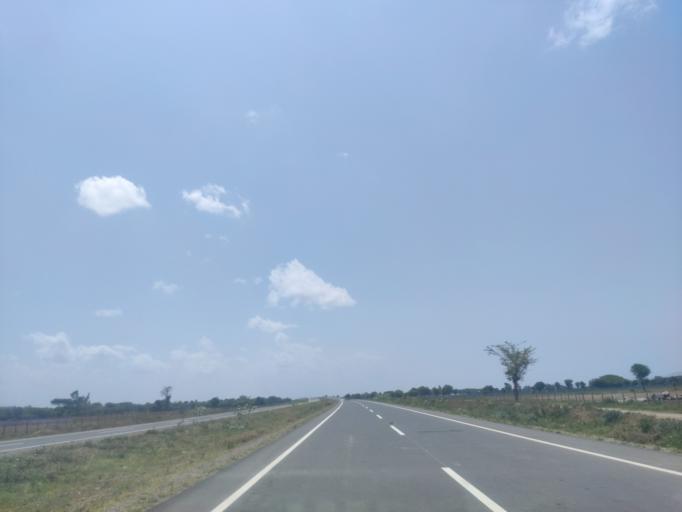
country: ET
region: Oromiya
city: Mojo
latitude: 8.3469
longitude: 38.9789
